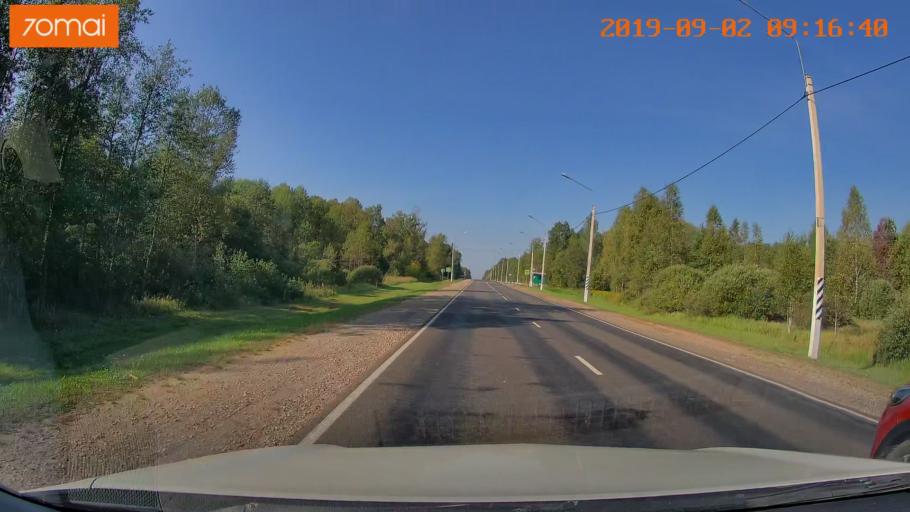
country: RU
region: Kaluga
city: Nikola-Lenivets
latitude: 54.8306
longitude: 35.4700
